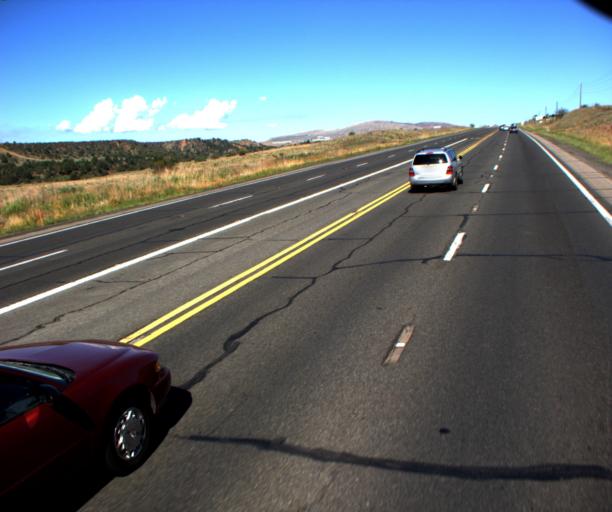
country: US
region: Arizona
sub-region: Yavapai County
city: Prescott Valley
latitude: 34.5745
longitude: -112.2824
